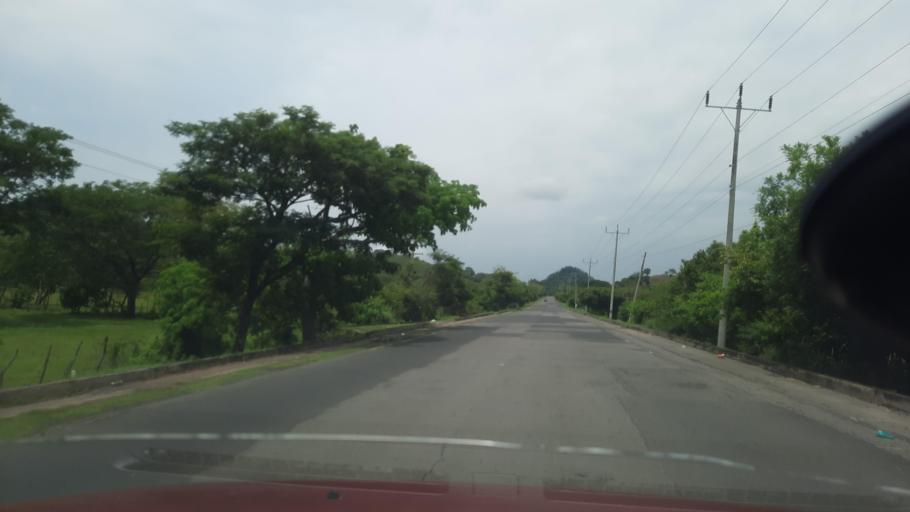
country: SV
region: La Union
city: Pasaquina
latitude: 13.6099
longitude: -87.8502
